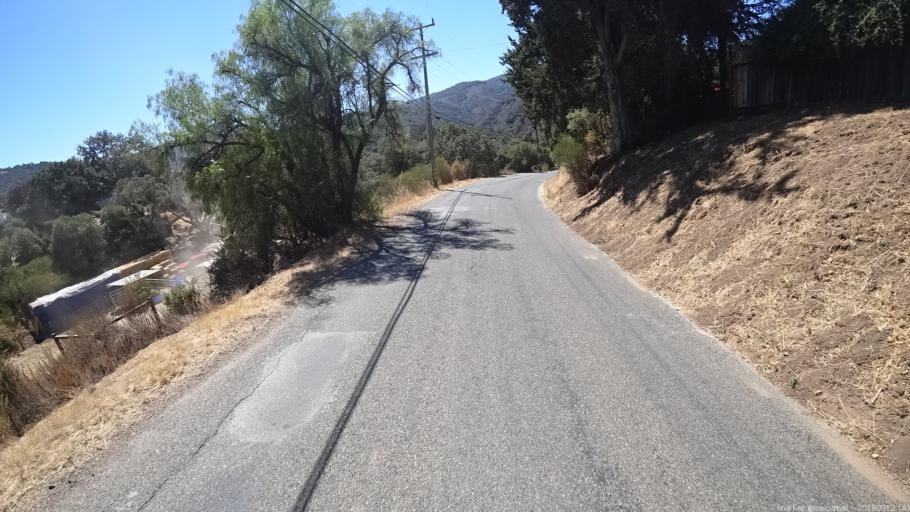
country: US
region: California
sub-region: Monterey County
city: Carmel Valley Village
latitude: 36.4772
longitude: -121.7216
